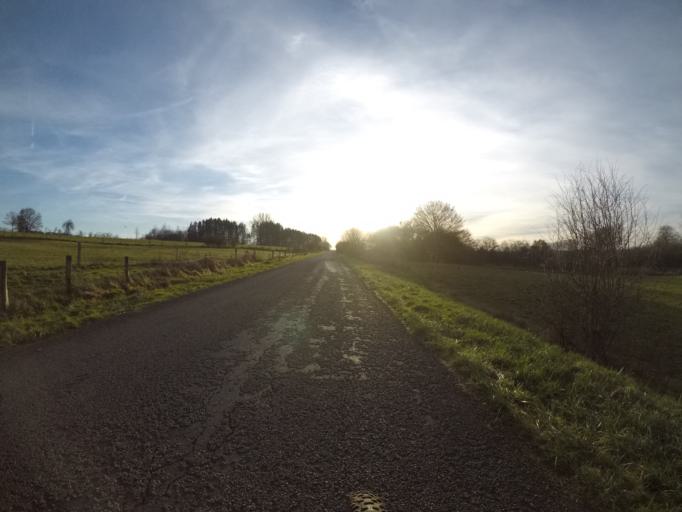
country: BE
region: Wallonia
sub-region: Province du Luxembourg
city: Tintigny
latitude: 49.6721
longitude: 5.4678
